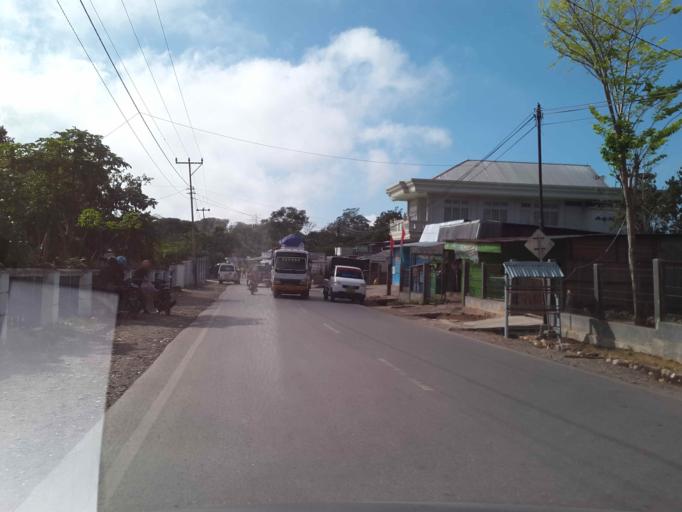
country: ID
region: East Nusa Tenggara
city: Rote
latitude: -9.8620
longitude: 124.2729
